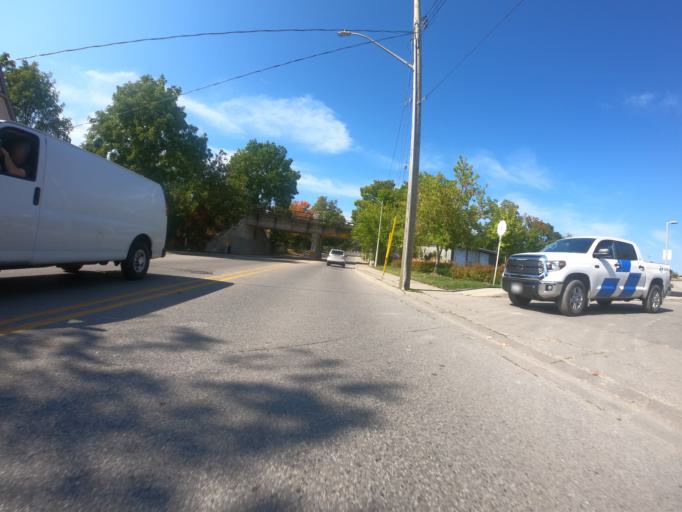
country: CA
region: Ontario
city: Waterloo
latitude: 43.4492
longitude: -80.5039
